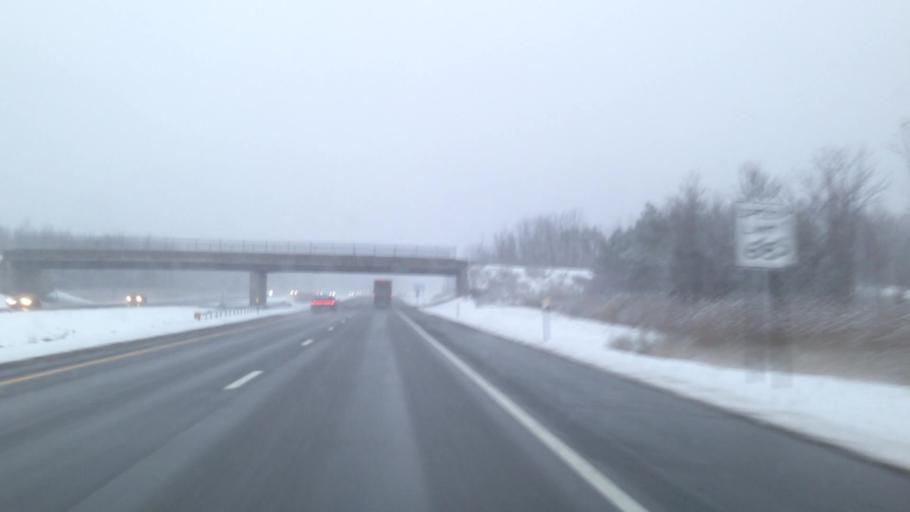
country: US
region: New York
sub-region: Onondaga County
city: Minoa
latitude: 43.0949
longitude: -76.0338
